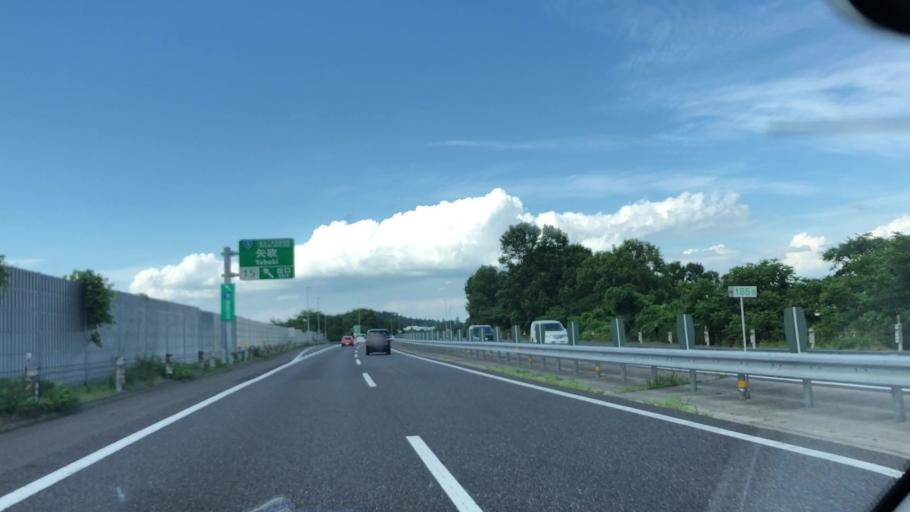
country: JP
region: Fukushima
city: Sukagawa
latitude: 37.1925
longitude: 140.2949
